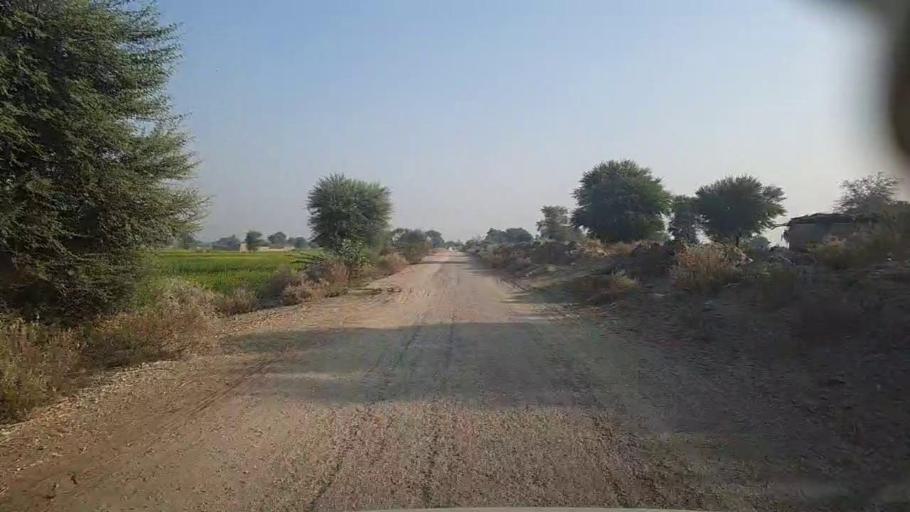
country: PK
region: Sindh
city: Karaundi
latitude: 26.7340
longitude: 68.4832
